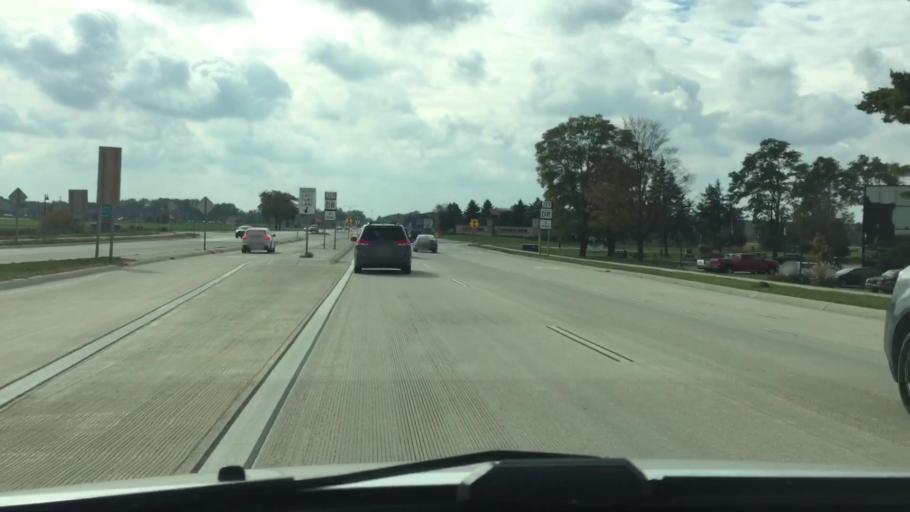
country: US
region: Wisconsin
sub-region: Waukesha County
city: Dousman
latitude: 43.0657
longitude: -88.4716
